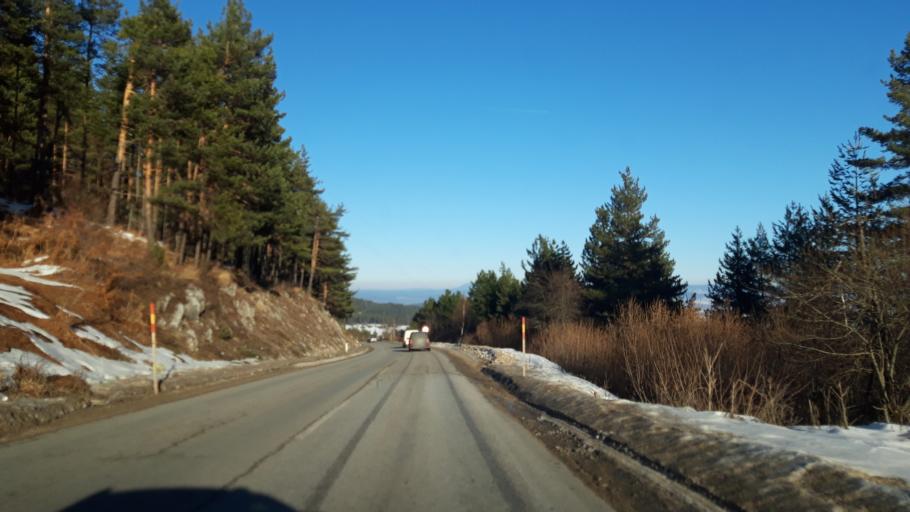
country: BA
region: Republika Srpska
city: Sokolac
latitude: 43.9101
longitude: 18.7165
